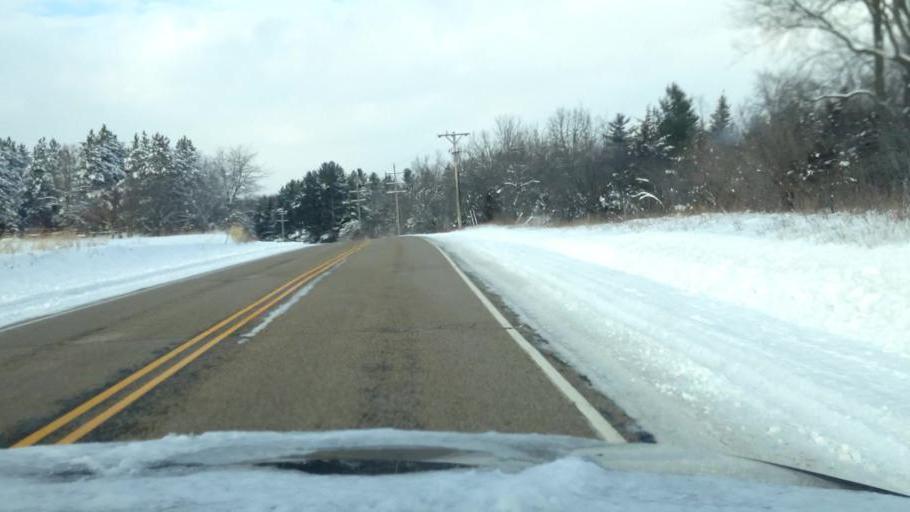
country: US
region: Wisconsin
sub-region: Walworth County
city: East Troy
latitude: 42.8312
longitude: -88.4239
